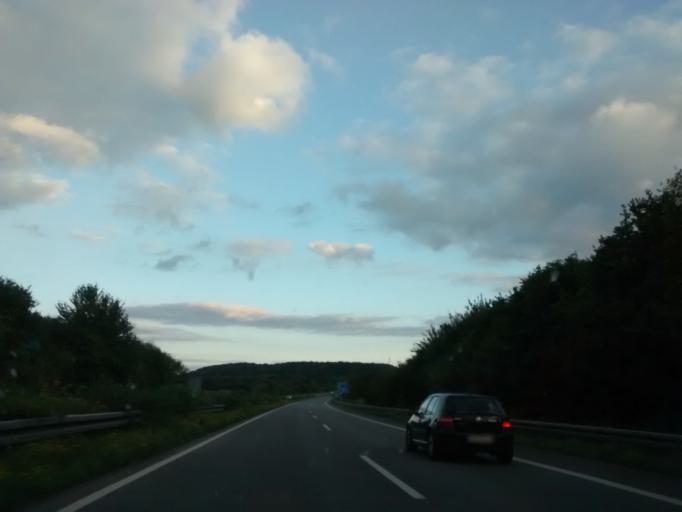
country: DE
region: Lower Saxony
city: Bissendorf
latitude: 52.2080
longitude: 8.1318
